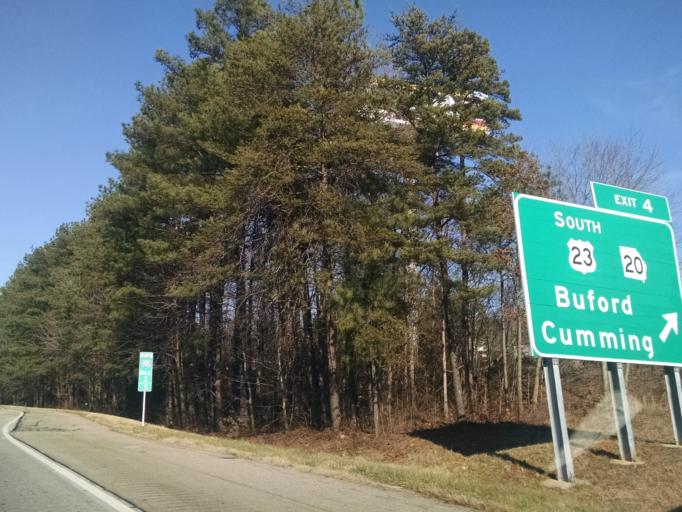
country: US
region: Georgia
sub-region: Gwinnett County
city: Buford
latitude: 34.0828
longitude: -83.9957
